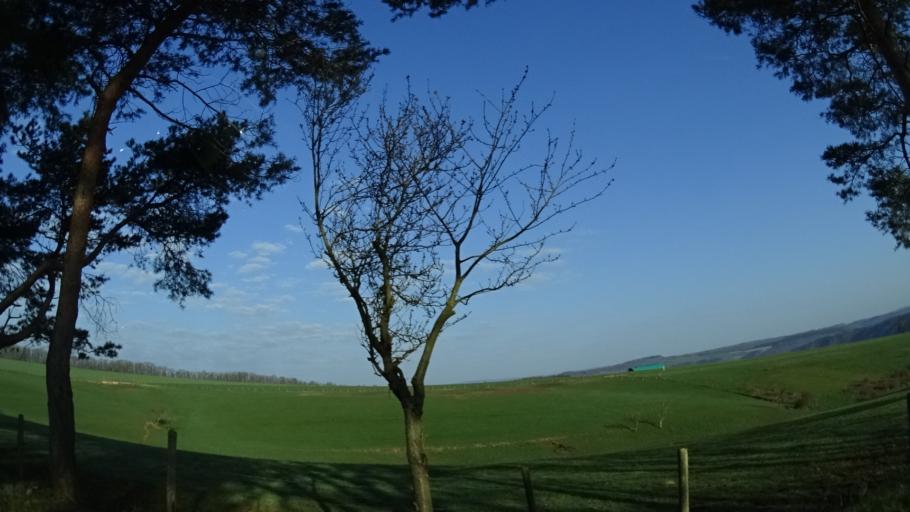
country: DE
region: Rheinland-Pfalz
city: Dickesbach
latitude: 49.7220
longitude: 7.4334
